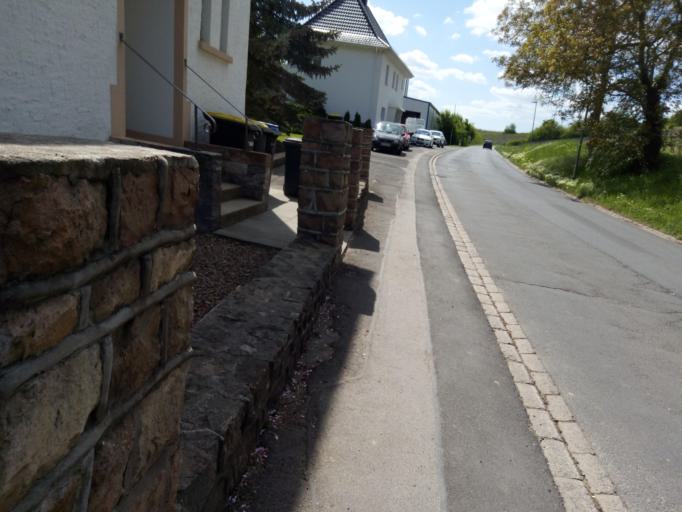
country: DE
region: Rheinland-Pfalz
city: Rummelsheim
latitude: 49.9286
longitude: 7.8641
